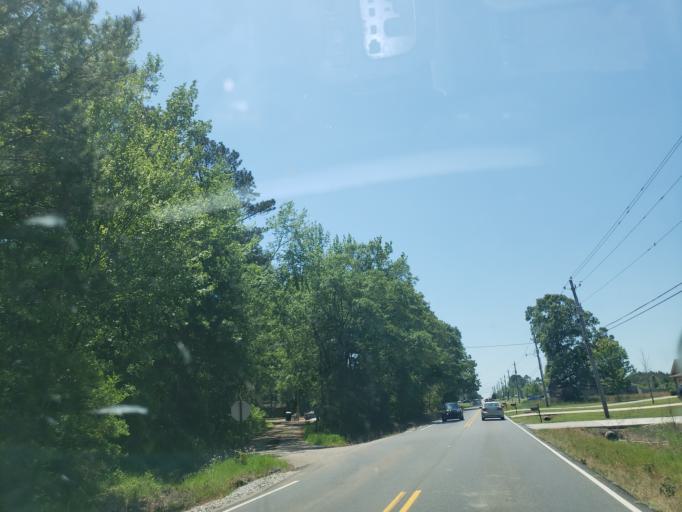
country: US
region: Alabama
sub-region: Madison County
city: Harvest
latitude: 34.8806
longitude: -86.7407
